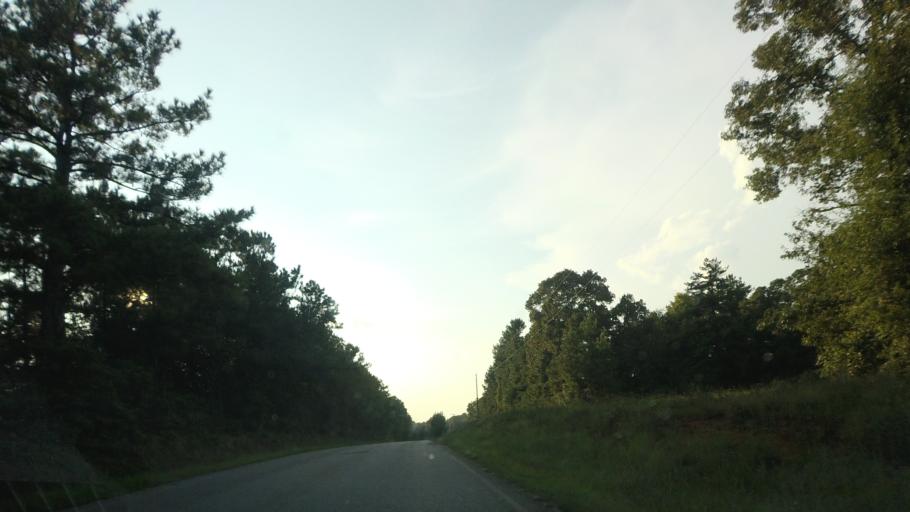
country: US
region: Georgia
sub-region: Bibb County
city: West Point
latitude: 32.9461
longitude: -83.7928
